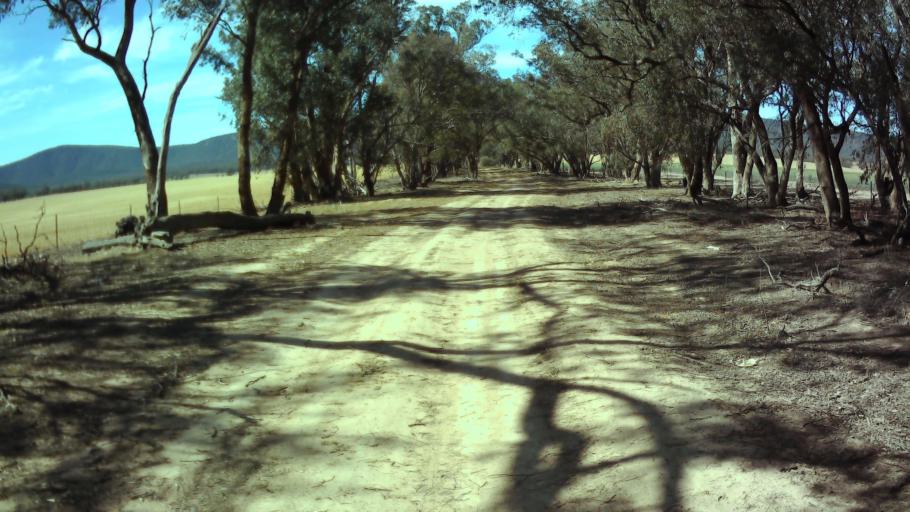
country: AU
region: New South Wales
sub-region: Weddin
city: Grenfell
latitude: -33.9396
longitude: 148.0479
